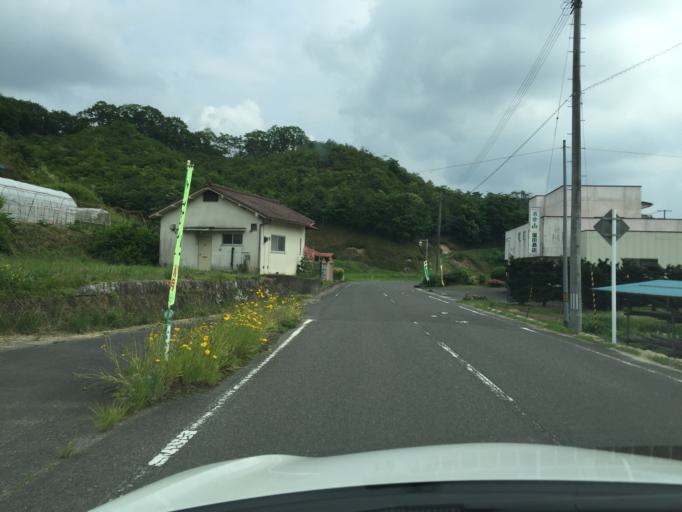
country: JP
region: Fukushima
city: Ishikawa
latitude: 37.2368
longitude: 140.4938
